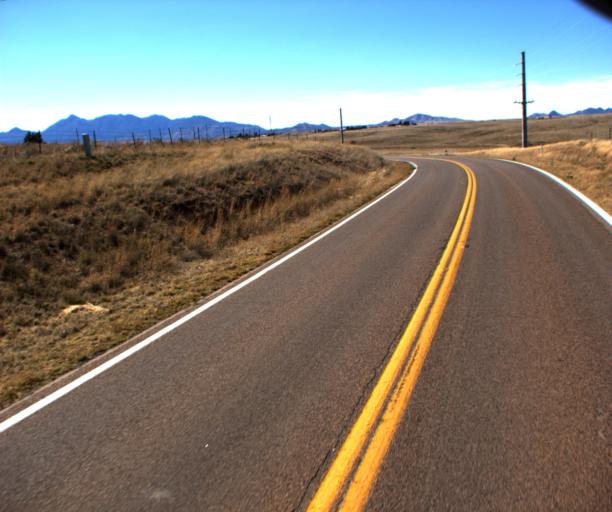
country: US
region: Arizona
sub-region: Cochise County
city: Huachuca City
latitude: 31.6746
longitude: -110.6377
